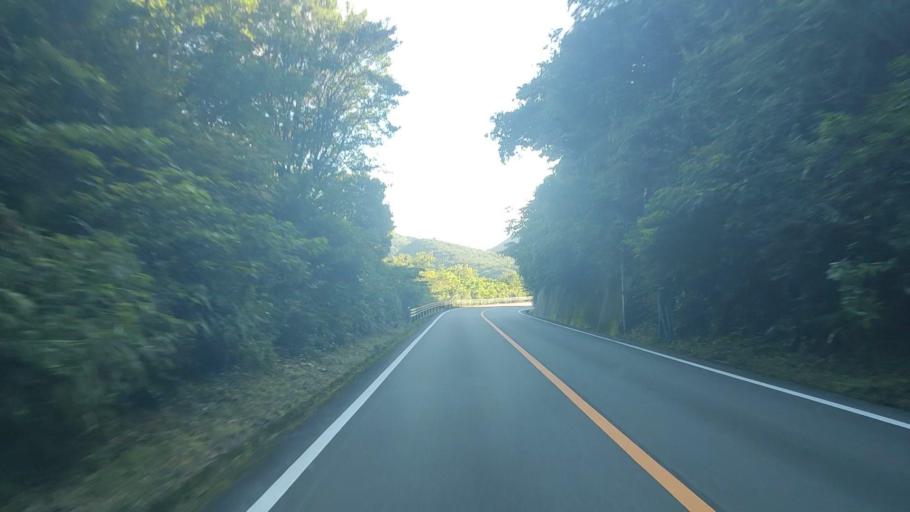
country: JP
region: Mie
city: Toba
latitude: 34.3989
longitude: 136.8661
